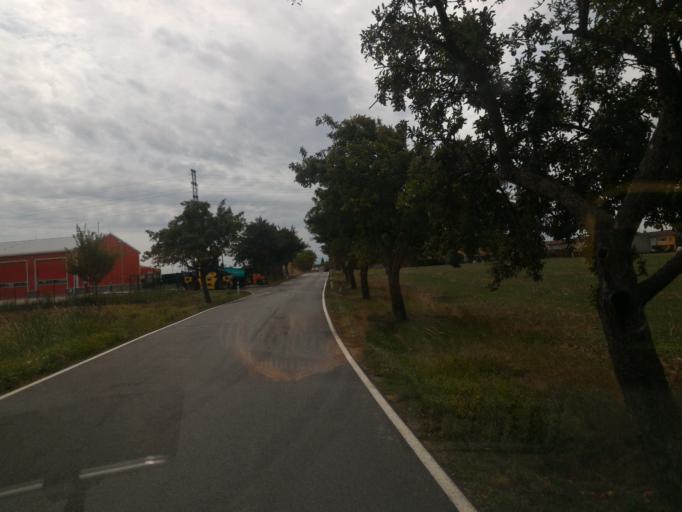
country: CZ
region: Jihocesky
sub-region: Okres Jindrichuv Hradec
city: Dacice
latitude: 49.0891
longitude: 15.4267
